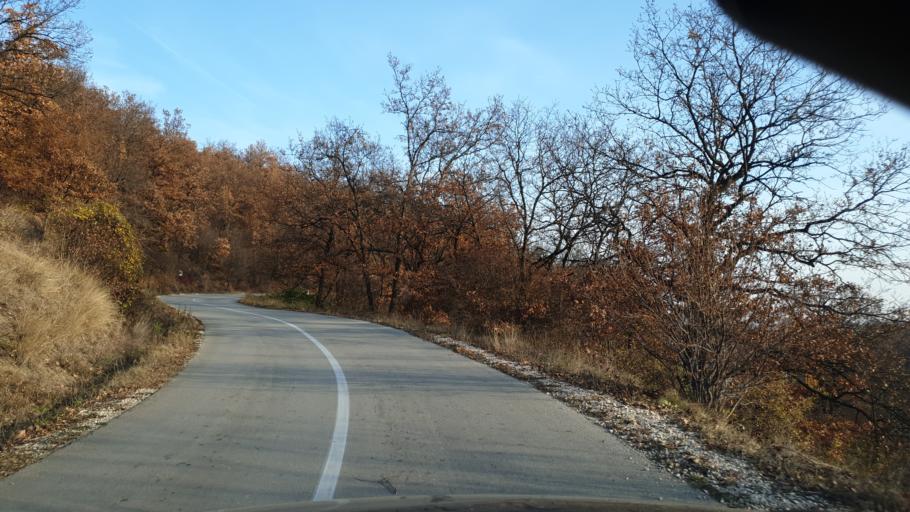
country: RS
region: Central Serbia
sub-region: Borski Okrug
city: Bor
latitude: 44.0480
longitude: 22.0765
